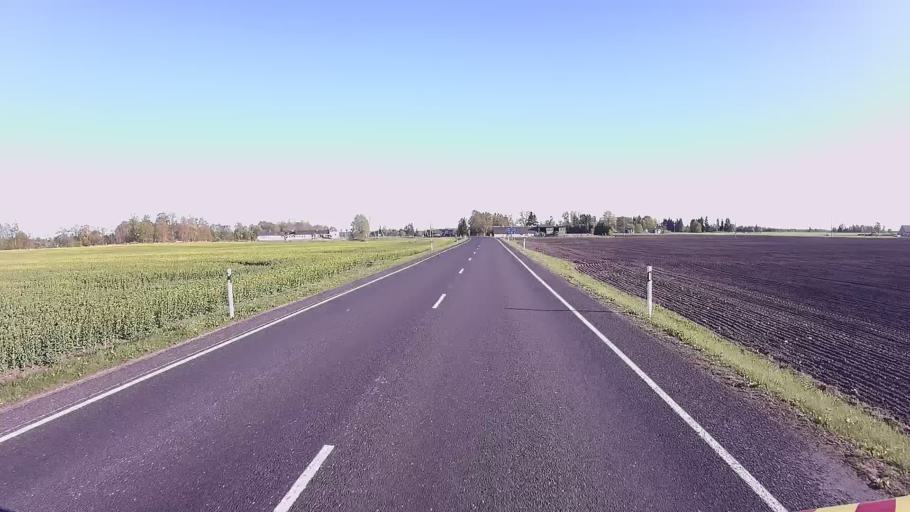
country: EE
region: Viljandimaa
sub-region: Vohma linn
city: Vohma
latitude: 58.6645
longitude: 25.6077
